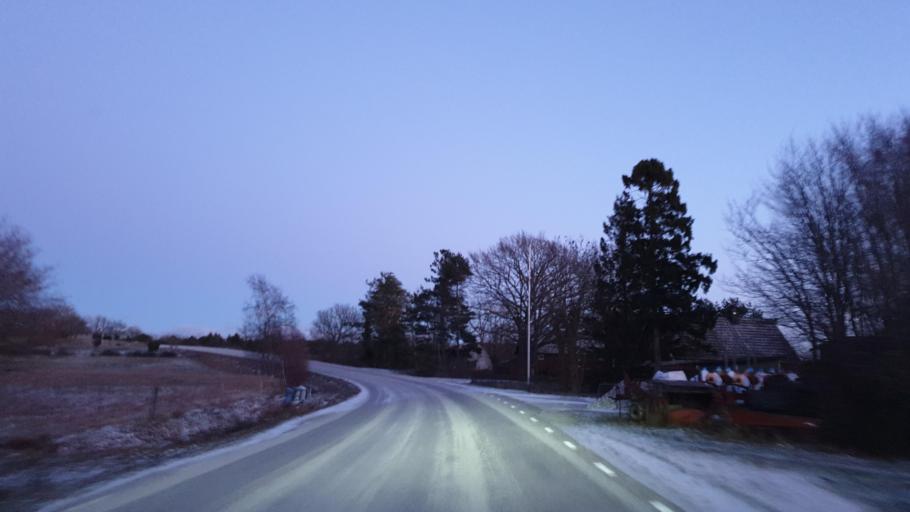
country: SE
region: Gotland
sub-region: Gotland
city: Slite
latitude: 57.4185
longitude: 18.8773
